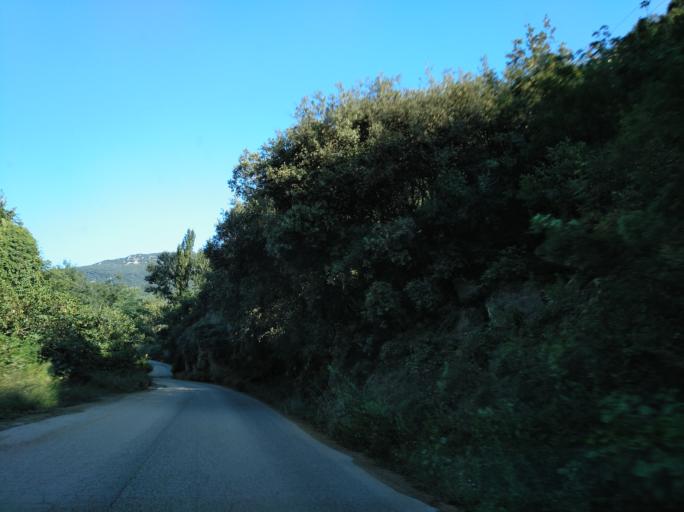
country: ES
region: Catalonia
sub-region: Provincia de Girona
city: la Cellera de Ter
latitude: 41.9820
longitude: 2.5878
